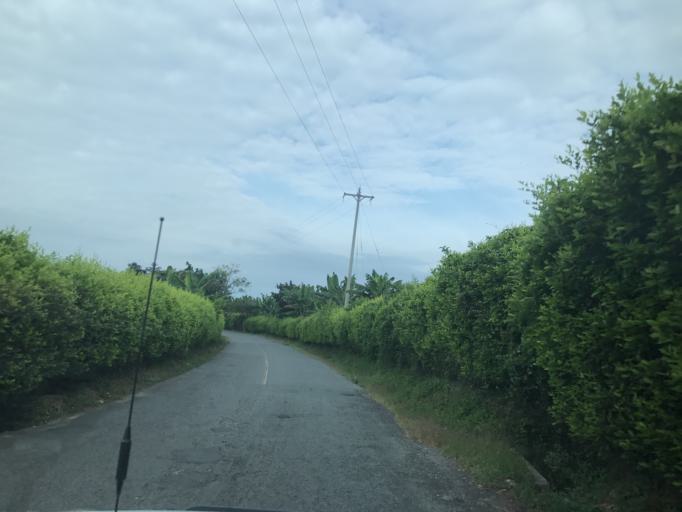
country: CO
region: Quindio
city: Montenegro
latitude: 4.5566
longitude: -75.7678
